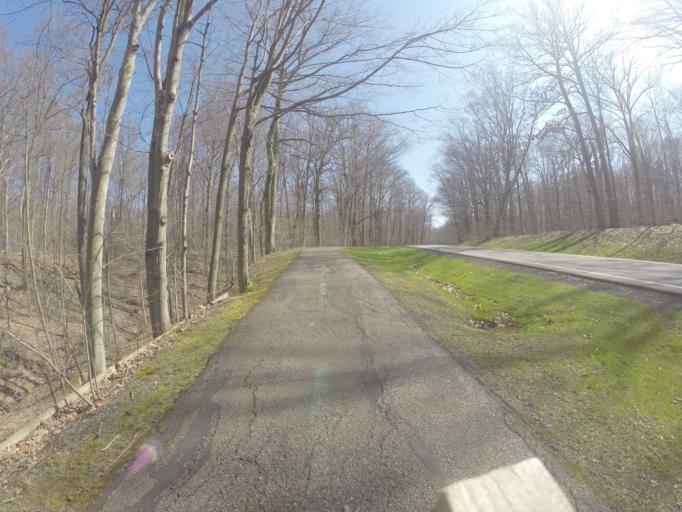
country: US
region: Ohio
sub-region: Lake County
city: Willoughby Hills
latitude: 41.5865
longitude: -81.4284
